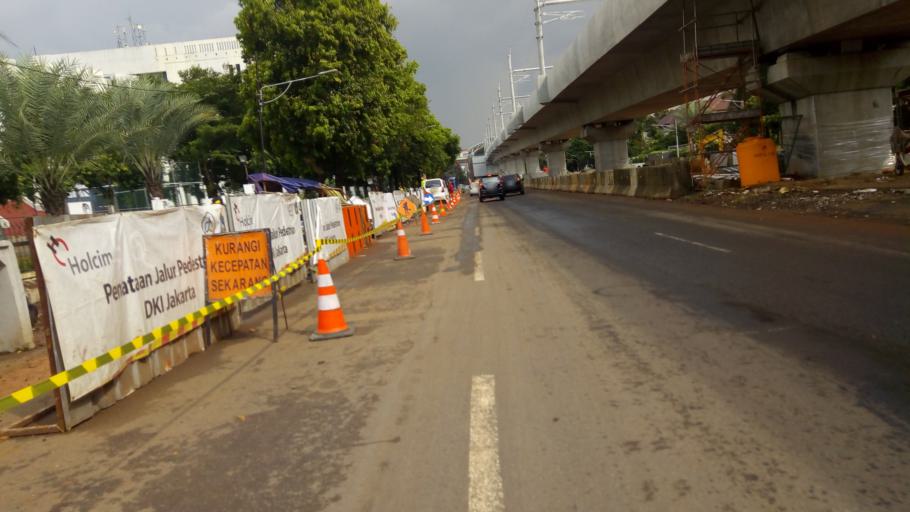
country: ID
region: Jakarta Raya
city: Jakarta
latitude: -6.2351
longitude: 106.7985
